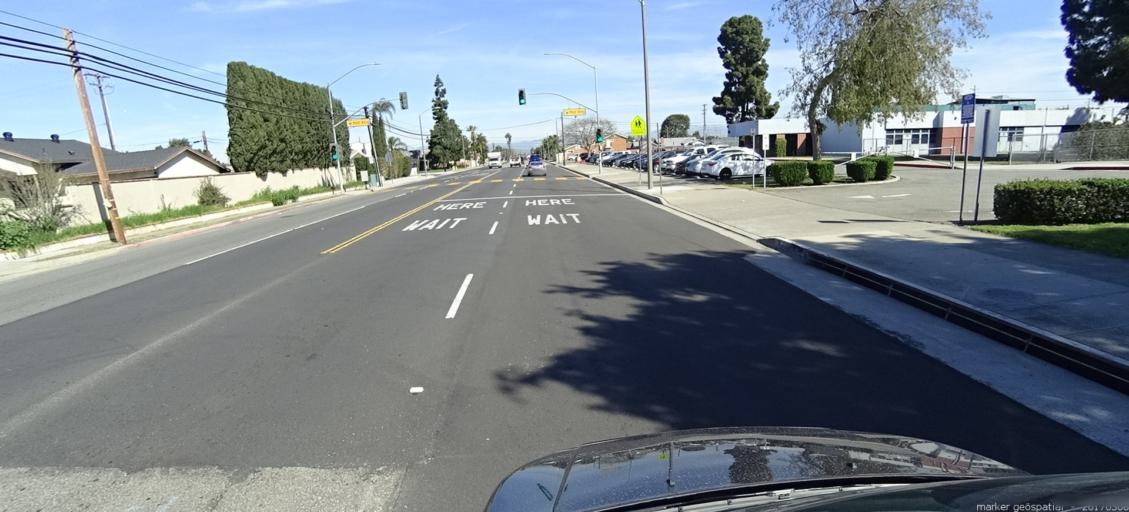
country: US
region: California
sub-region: Orange County
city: Stanton
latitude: 33.8196
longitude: -117.9846
